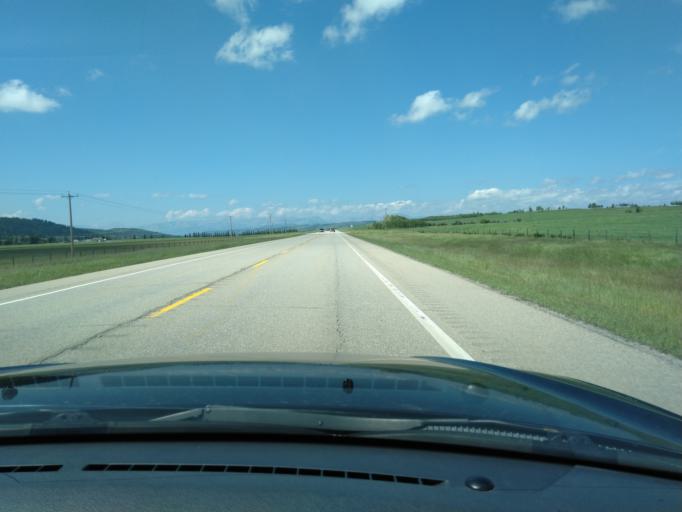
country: CA
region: Alberta
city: Cochrane
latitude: 51.2241
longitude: -114.6565
